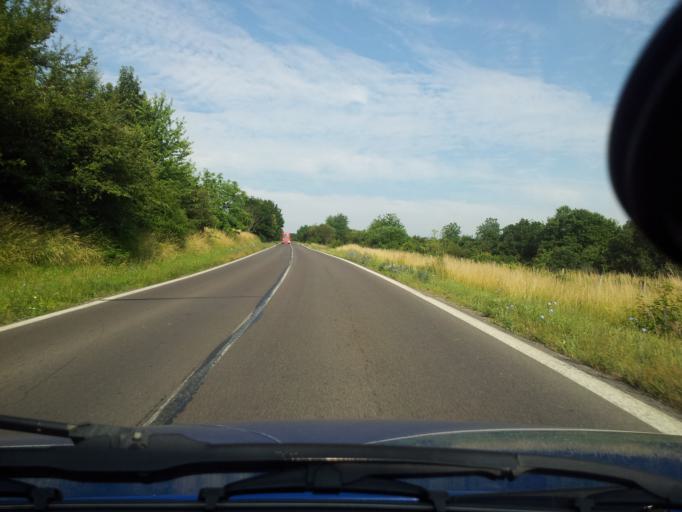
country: SK
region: Nitriansky
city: Banovce nad Bebravou
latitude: 48.6946
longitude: 18.3045
